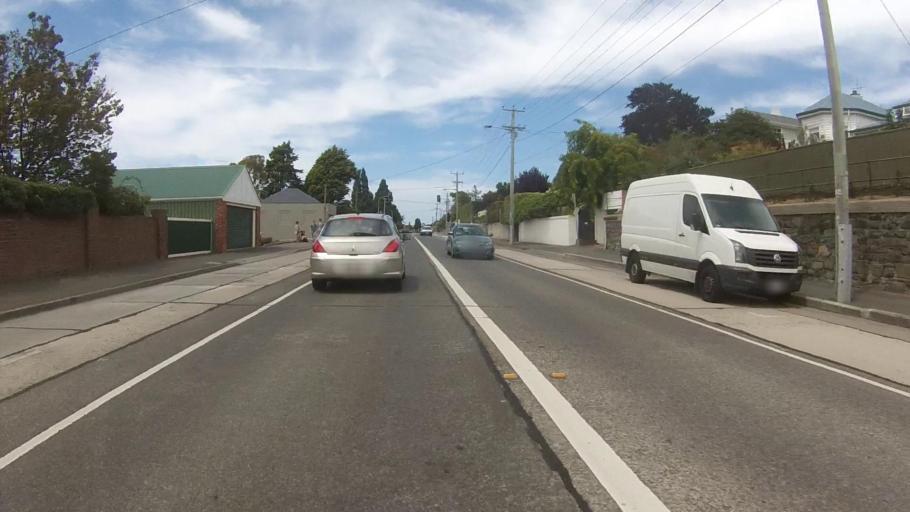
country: AU
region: Tasmania
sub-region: Hobart
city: Sandy Bay
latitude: -42.9093
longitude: 147.3479
